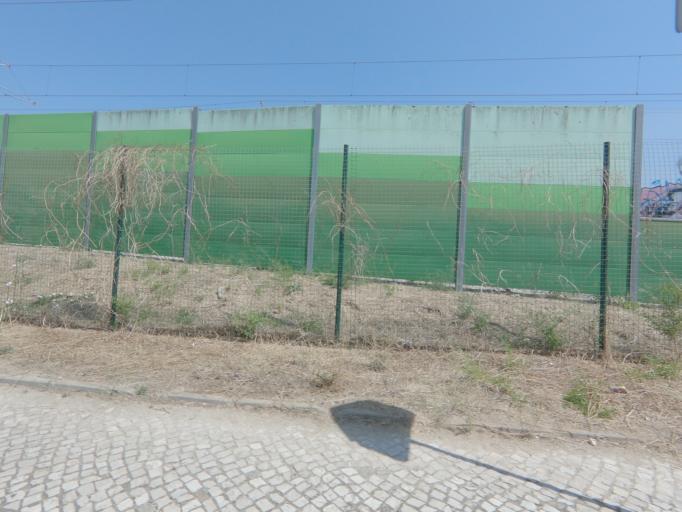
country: PT
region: Setubal
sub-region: Setubal
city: Setubal
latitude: 38.5383
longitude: -8.8831
